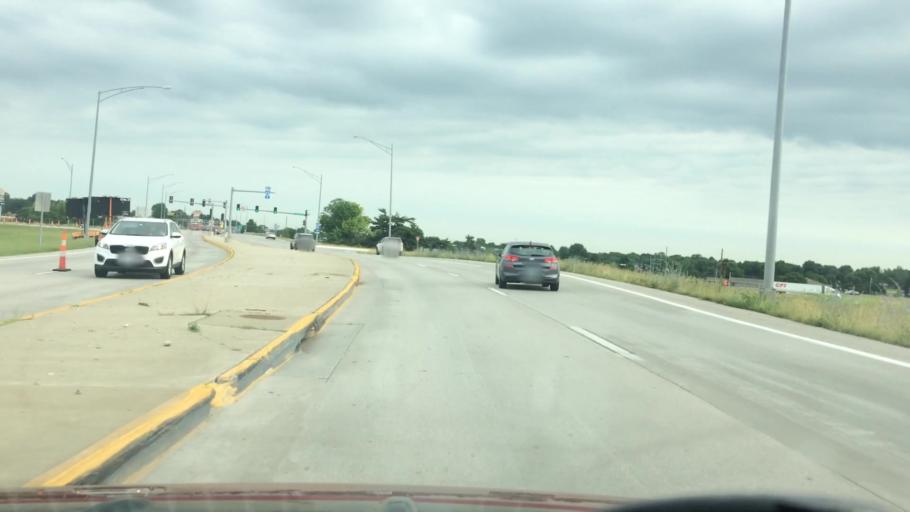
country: US
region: Missouri
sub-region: Greene County
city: Springfield
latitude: 37.2475
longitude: -93.2609
